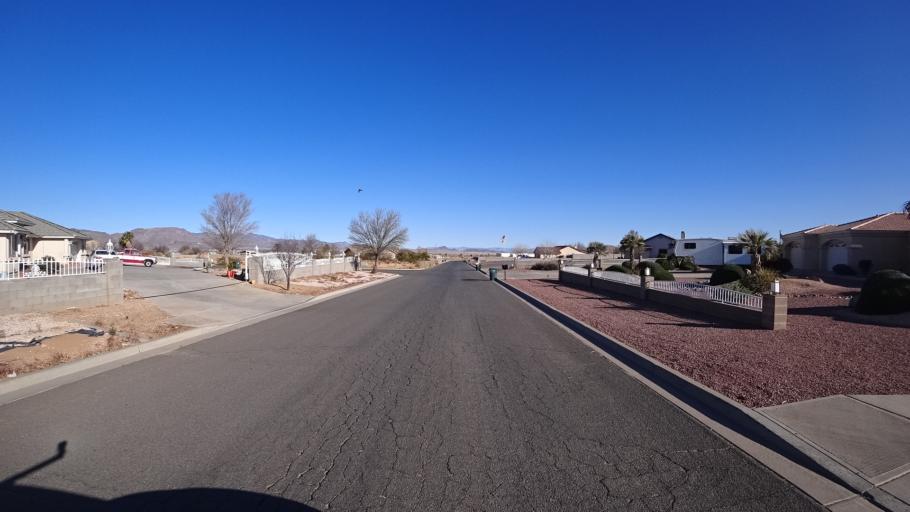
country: US
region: Arizona
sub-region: Mohave County
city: Kingman
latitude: 35.2080
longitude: -113.9985
